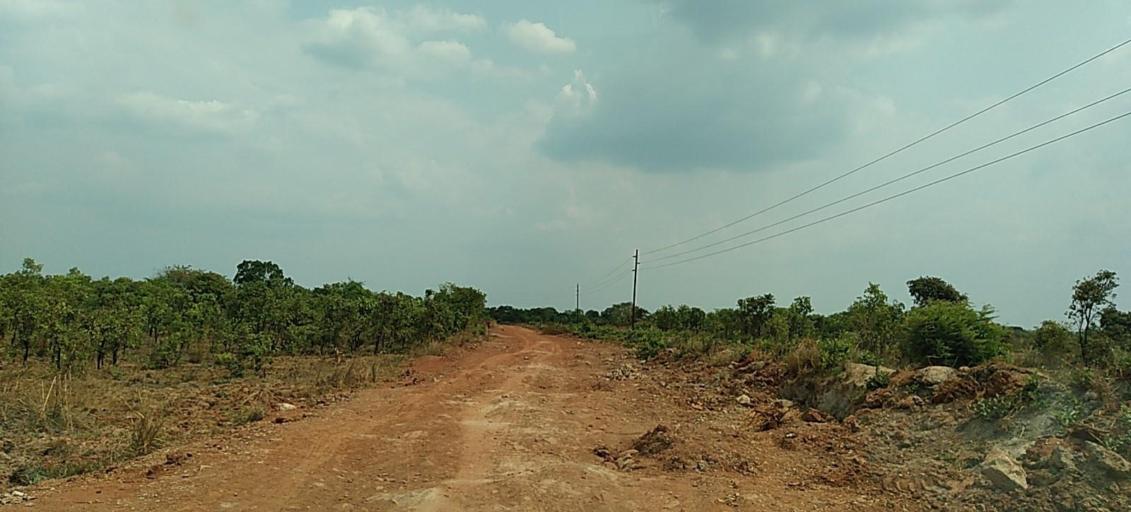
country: ZM
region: Copperbelt
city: Kalulushi
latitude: -12.8878
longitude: 28.0747
